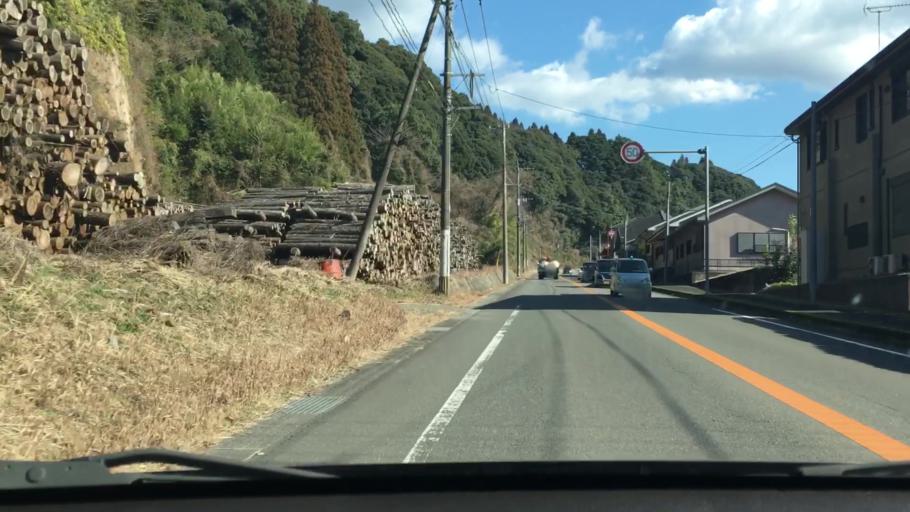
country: JP
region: Kagoshima
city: Satsumasendai
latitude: 31.7987
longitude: 130.4163
